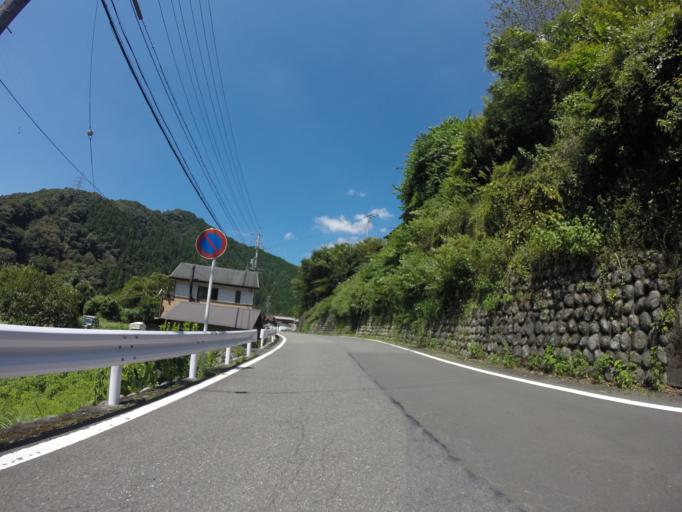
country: JP
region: Shizuoka
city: Shizuoka-shi
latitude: 35.0351
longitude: 138.2594
